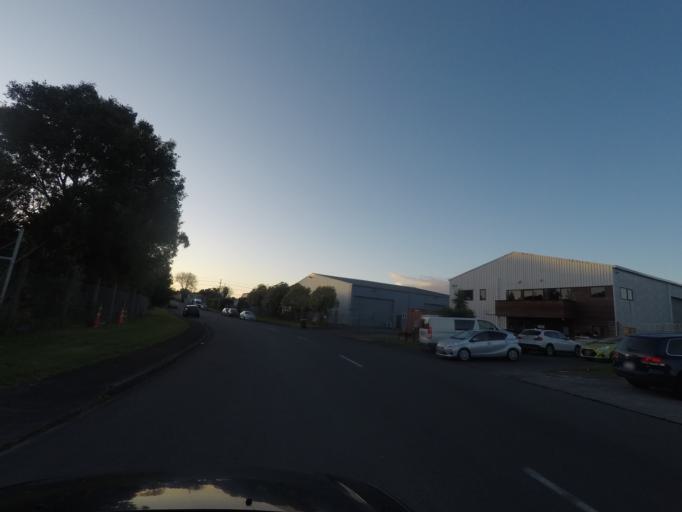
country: NZ
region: Auckland
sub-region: Auckland
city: Rosebank
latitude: -36.8902
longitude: 174.6590
